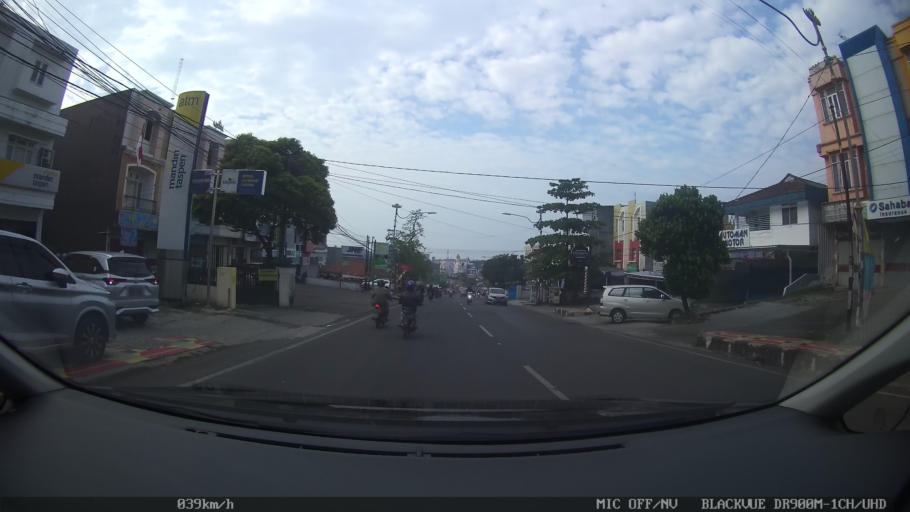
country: ID
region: Lampung
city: Bandarlampung
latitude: -5.4381
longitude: 105.2655
